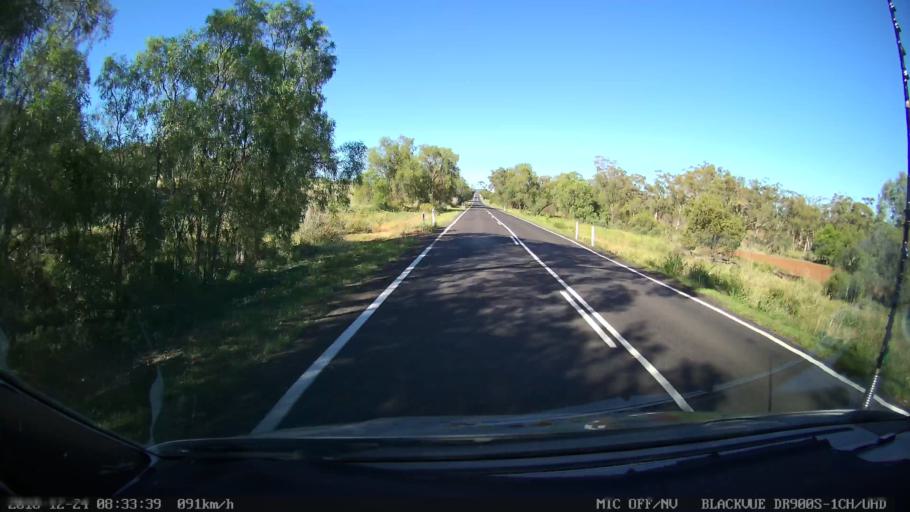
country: AU
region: New South Wales
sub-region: Liverpool Plains
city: Quirindi
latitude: -31.2876
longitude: 150.6816
